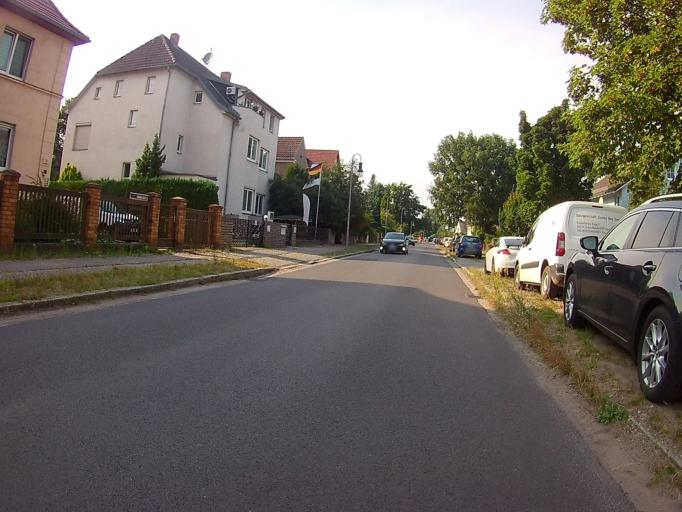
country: DE
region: Berlin
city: Kopenick Bezirk
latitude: 52.4635
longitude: 13.5715
